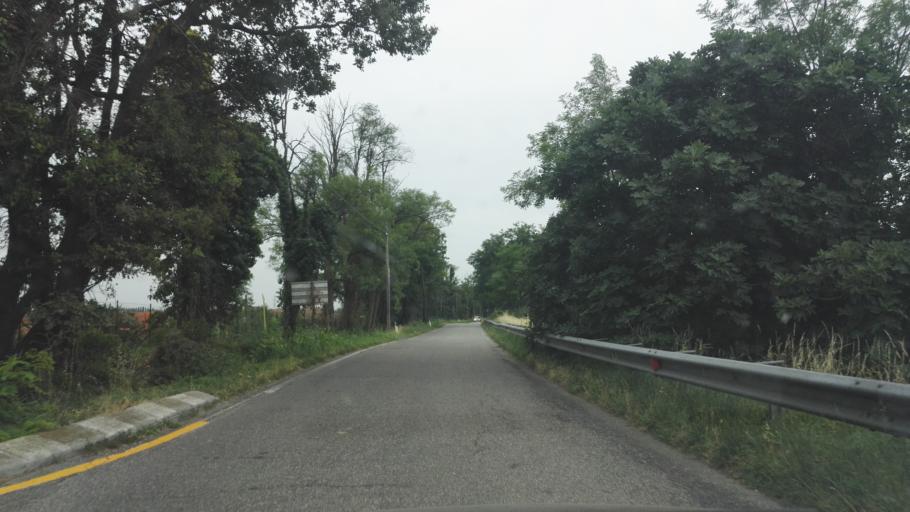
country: IT
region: Lombardy
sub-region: Citta metropolitana di Milano
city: San Bovio-San Felice
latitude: 45.4529
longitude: 9.3139
